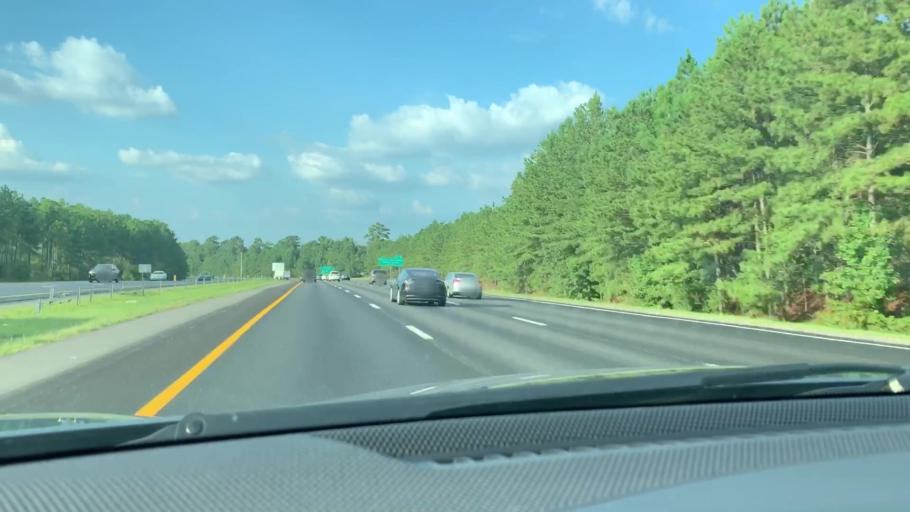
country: US
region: South Carolina
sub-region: Richland County
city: Forest Acres
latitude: 33.9854
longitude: -80.9531
